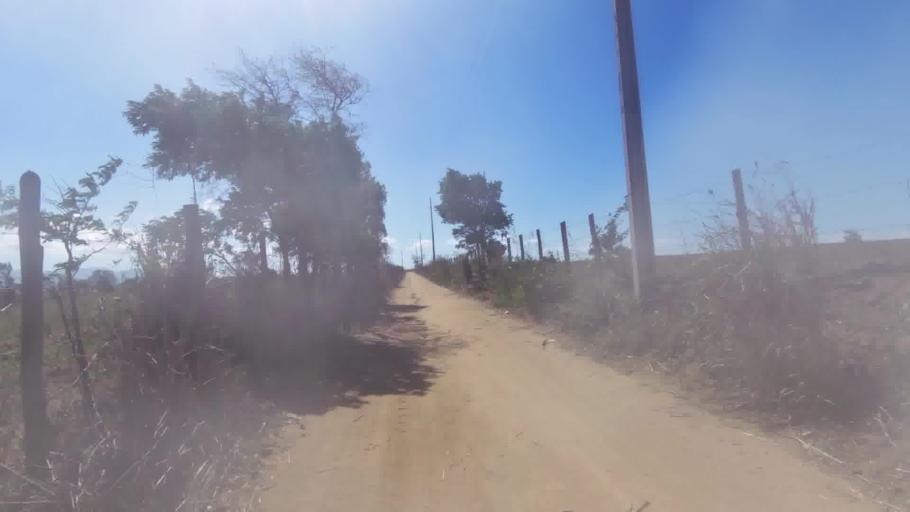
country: BR
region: Espirito Santo
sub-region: Marataizes
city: Marataizes
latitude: -21.1575
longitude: -40.9652
